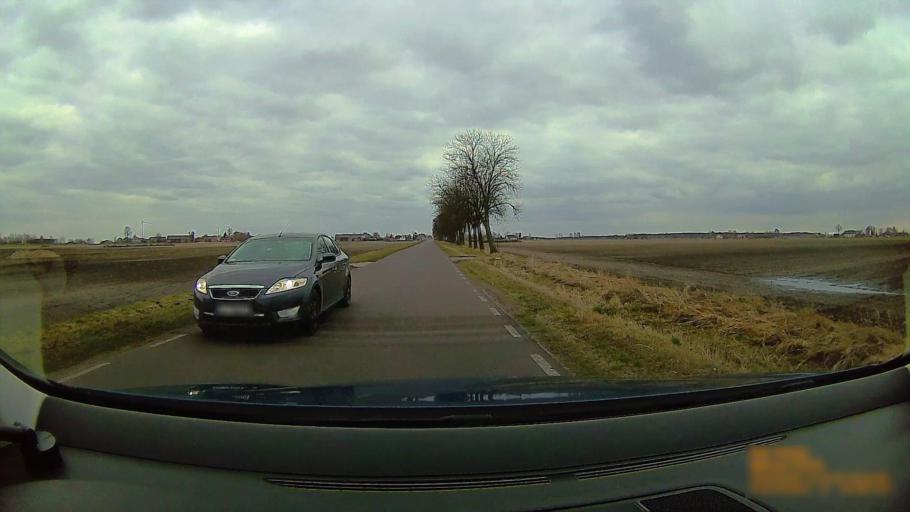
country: PL
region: Greater Poland Voivodeship
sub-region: Powiat koninski
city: Rychwal
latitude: 52.0999
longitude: 18.1024
